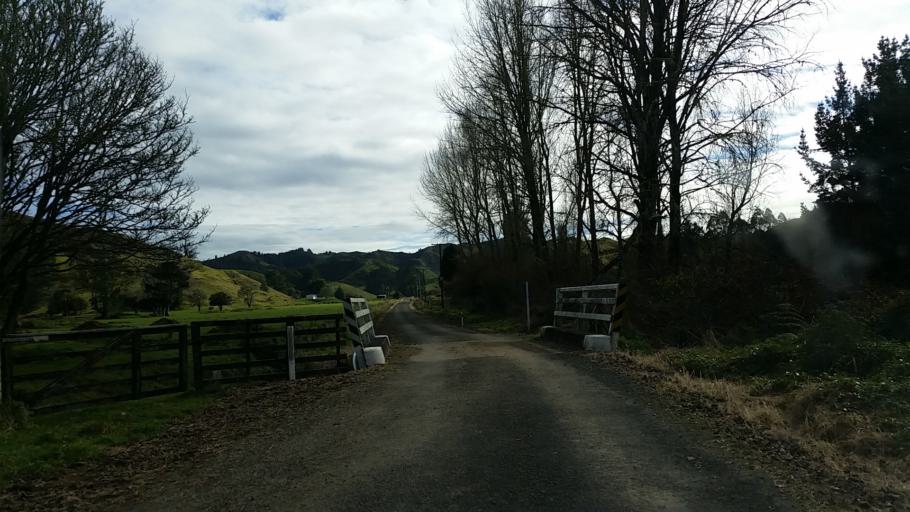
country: NZ
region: Taranaki
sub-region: South Taranaki District
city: Eltham
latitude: -39.2348
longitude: 174.5690
